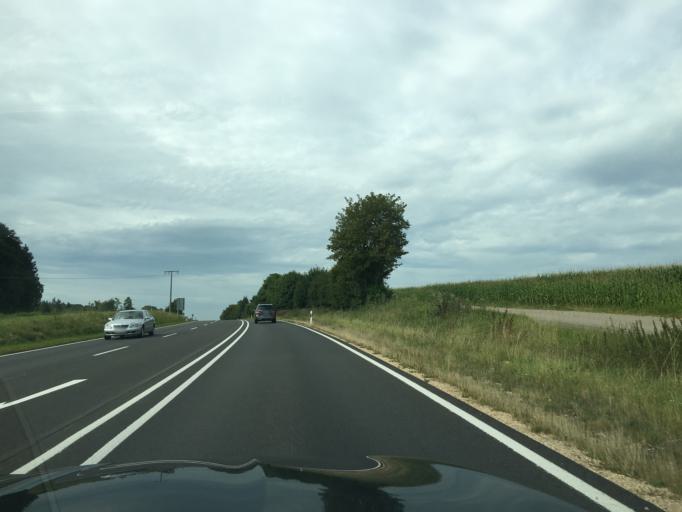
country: DE
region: Baden-Wuerttemberg
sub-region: Tuebingen Region
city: Rechtenstein
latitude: 48.2281
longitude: 9.5534
